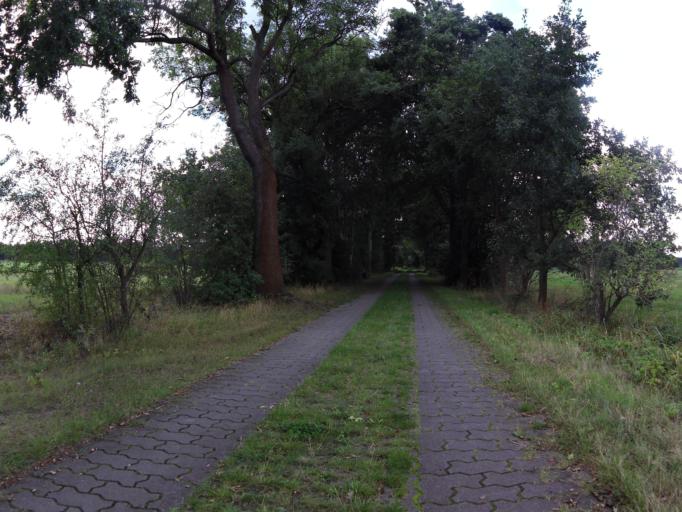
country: DE
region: Brandenburg
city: Storkow
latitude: 52.2362
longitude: 13.8762
